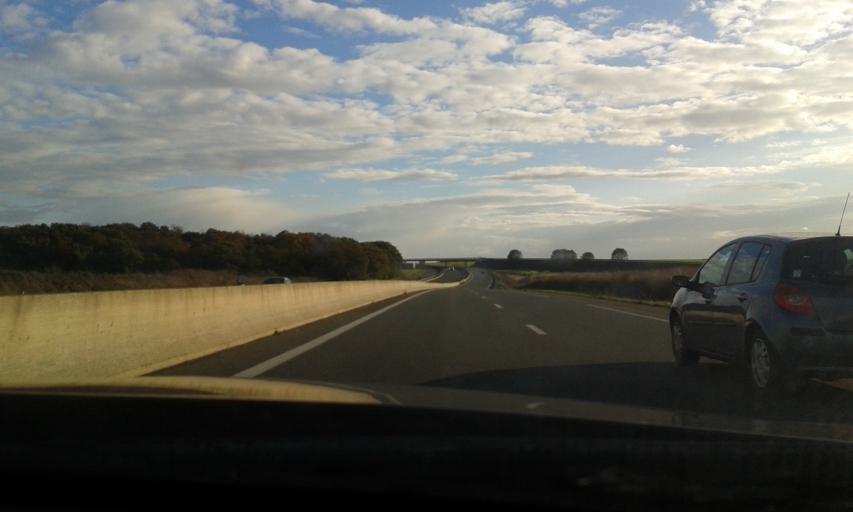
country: FR
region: Centre
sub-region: Departement d'Eure-et-Loir
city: Villemeux-sur-Eure
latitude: 48.6018
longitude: 1.4221
